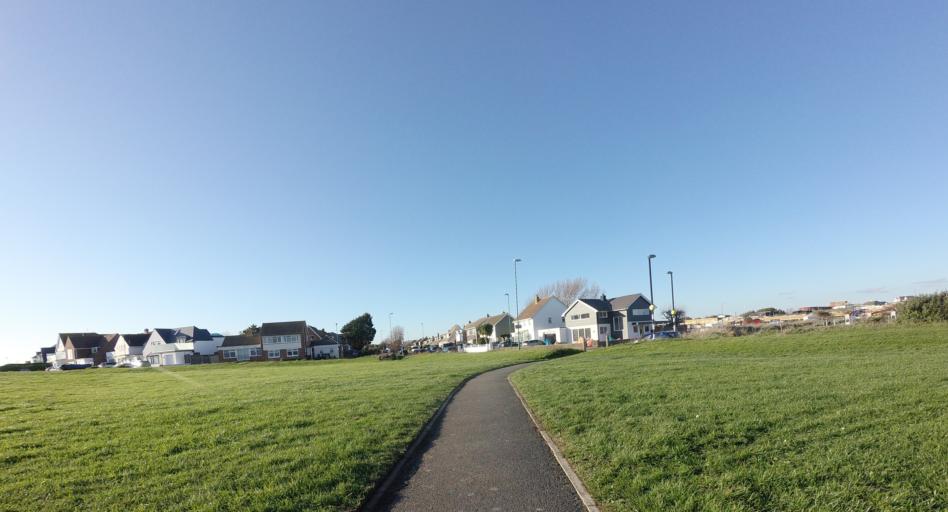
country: GB
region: England
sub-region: West Sussex
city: Shoreham-by-Sea
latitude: 50.8275
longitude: -0.2794
